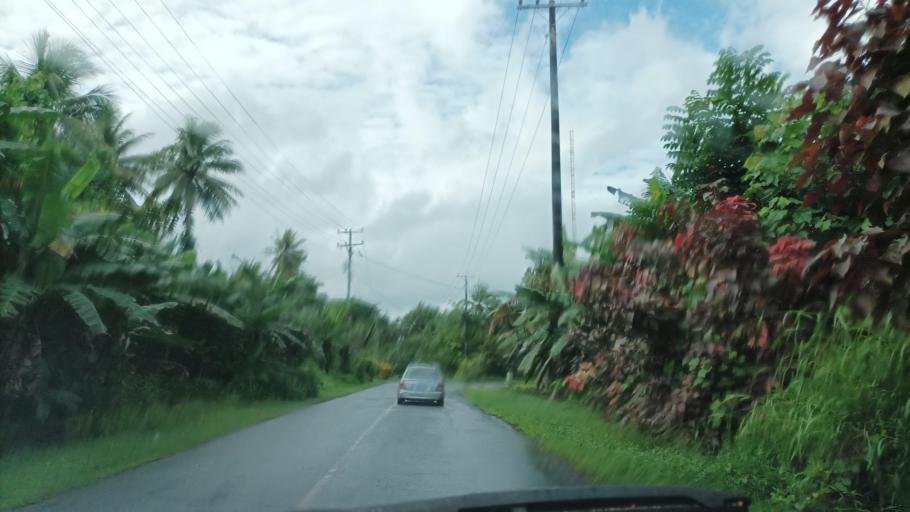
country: FM
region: Pohnpei
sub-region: Kolonia Municipality
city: Kolonia Town
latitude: 6.9504
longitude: 158.1947
